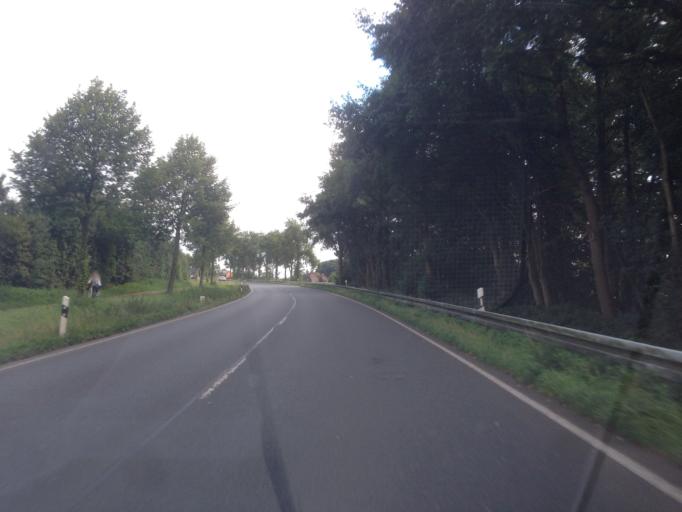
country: DE
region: North Rhine-Westphalia
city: Olfen
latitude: 51.7770
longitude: 7.3710
